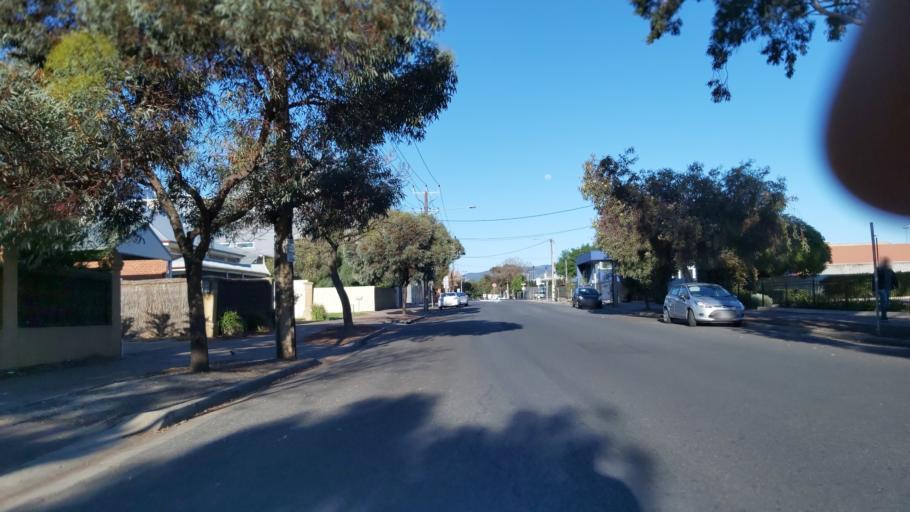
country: AU
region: South Australia
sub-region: Unley
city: Wayville
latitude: -34.9431
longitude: 138.5875
